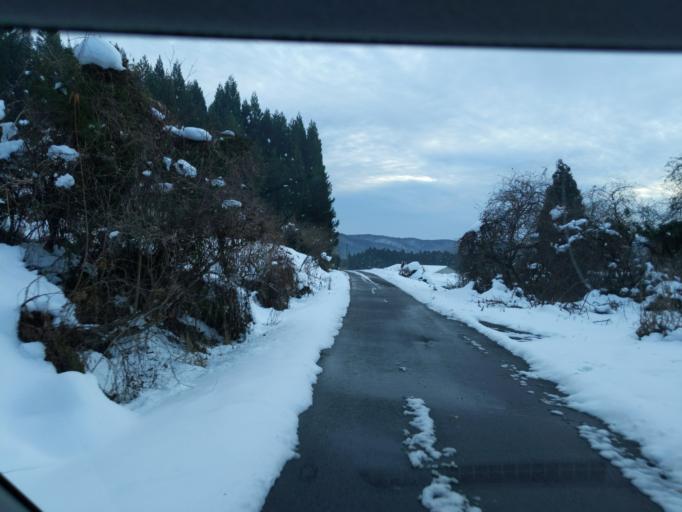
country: JP
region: Iwate
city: Mizusawa
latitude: 39.0506
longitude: 141.0577
